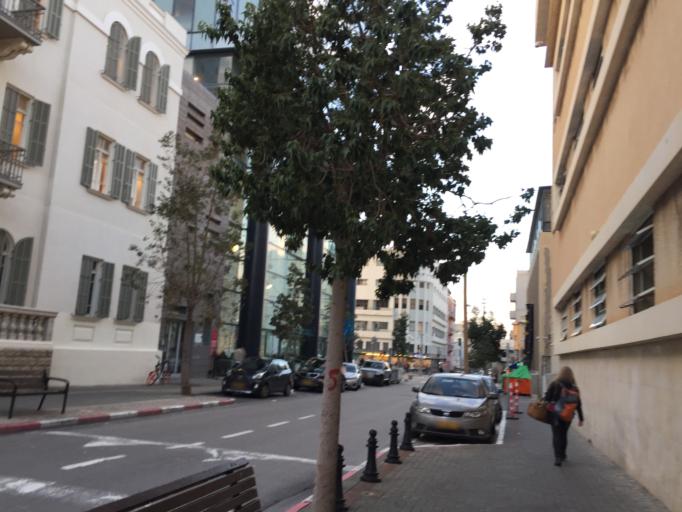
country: IL
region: Tel Aviv
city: Tel Aviv
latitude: 32.0625
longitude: 34.7720
